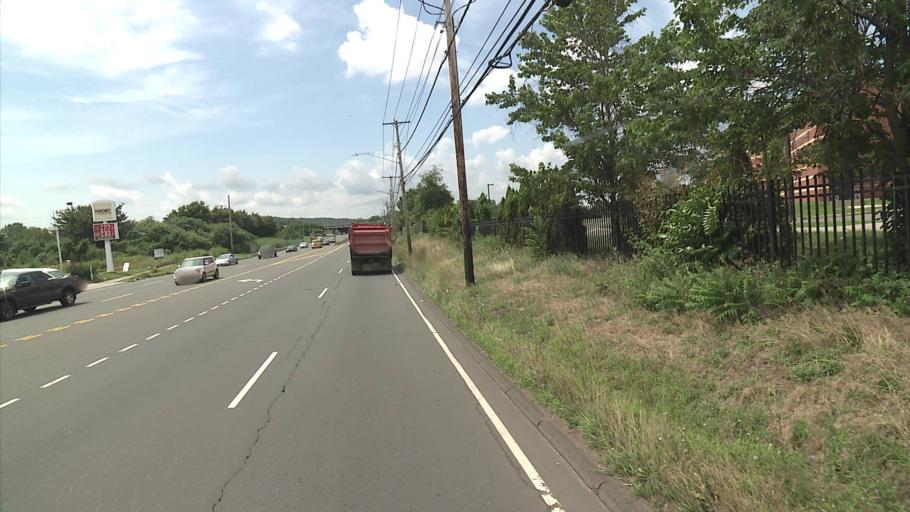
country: US
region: Connecticut
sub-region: New Haven County
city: East Haven
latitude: 41.3227
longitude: -72.8785
